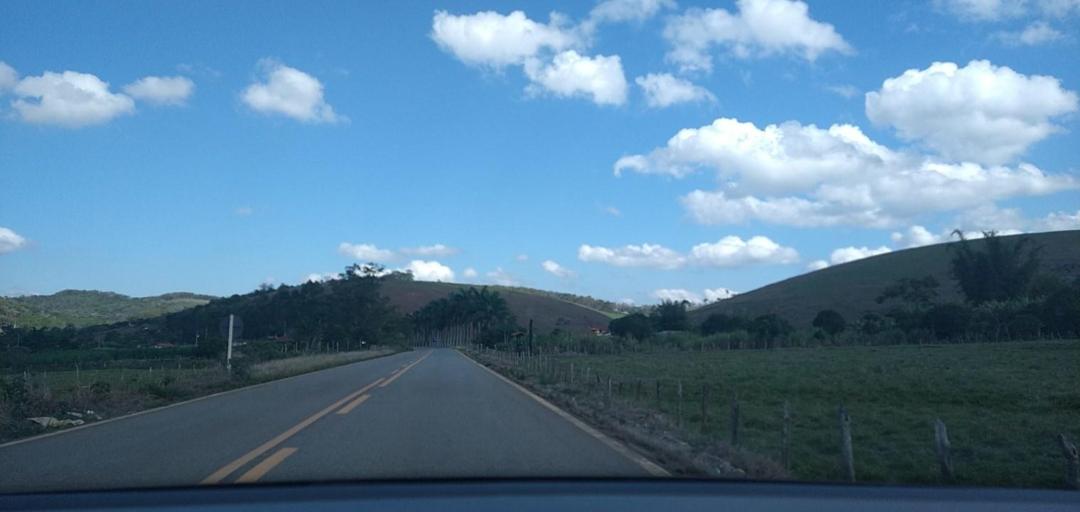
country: BR
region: Minas Gerais
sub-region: Alvinopolis
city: Alvinopolis
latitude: -20.0250
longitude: -43.0613
